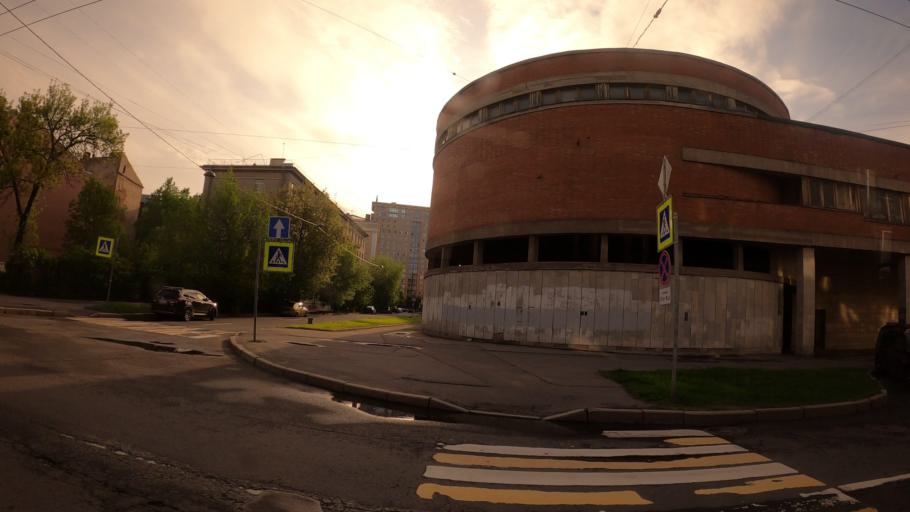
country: RU
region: St.-Petersburg
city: Vasyl'evsky Ostrov
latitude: 59.9310
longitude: 30.2493
